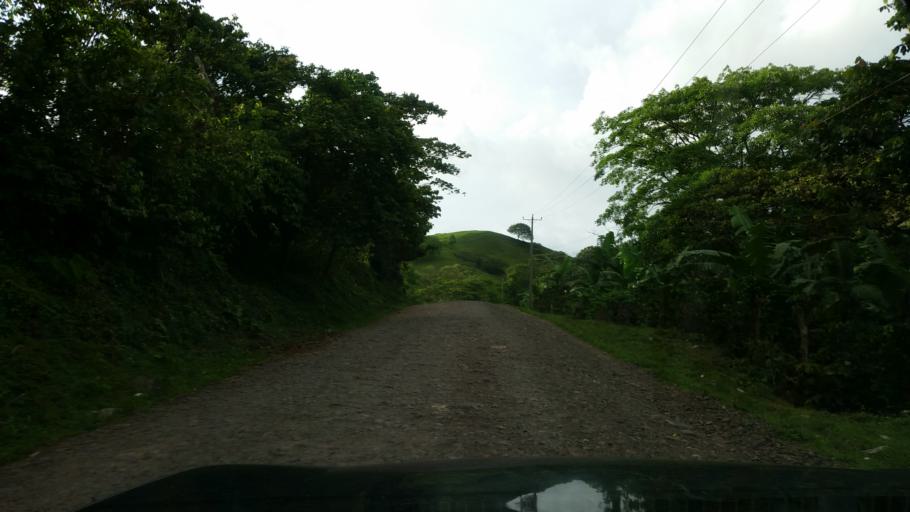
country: NI
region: Jinotega
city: Jinotega
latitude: 13.2361
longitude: -85.7290
